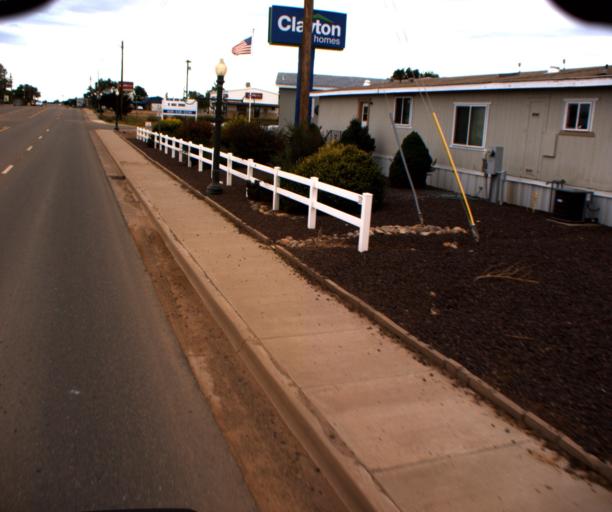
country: US
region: Arizona
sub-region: Navajo County
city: Snowflake
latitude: 34.5032
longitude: -110.0791
